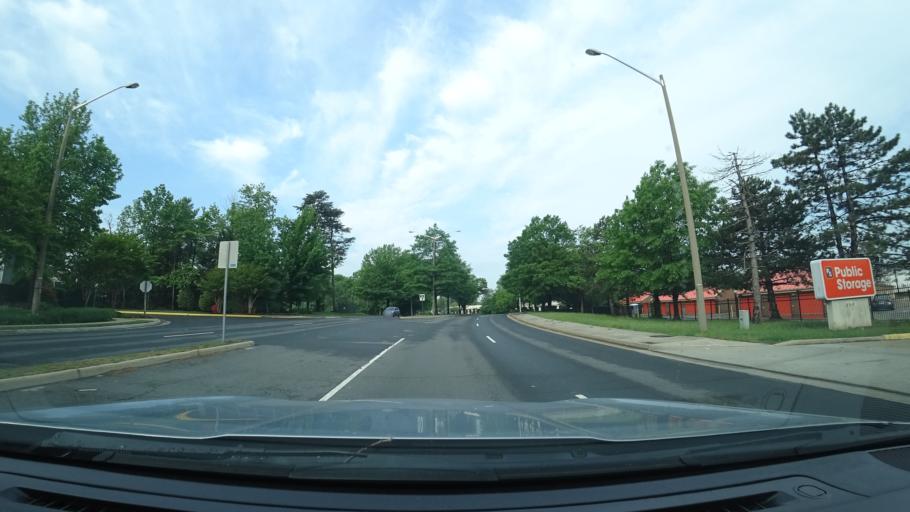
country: US
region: Virginia
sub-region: Fairfax County
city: Herndon
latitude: 38.9569
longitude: -77.3766
